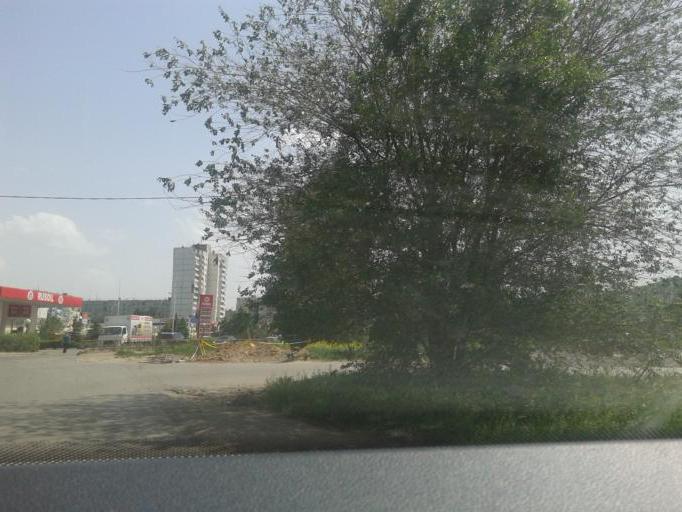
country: RU
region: Volgograd
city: Volgograd
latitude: 48.7604
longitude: 44.4992
